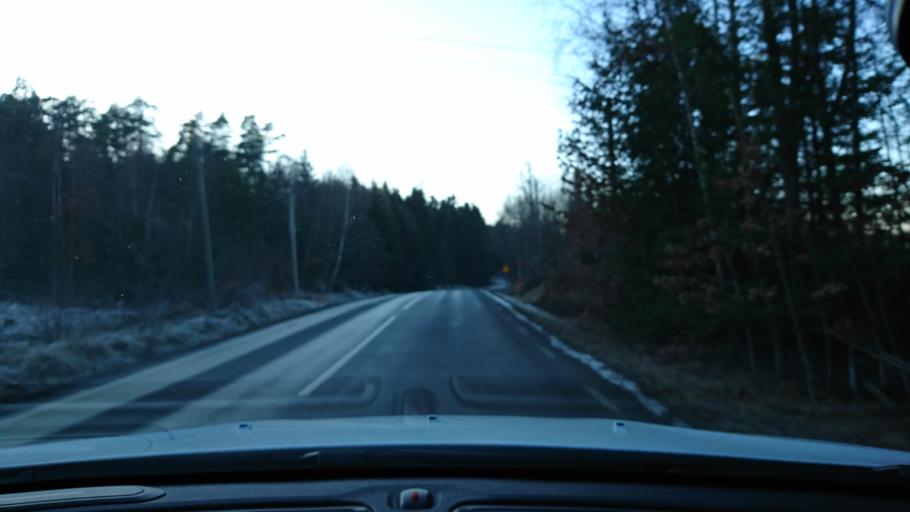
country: SE
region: Vaestra Goetaland
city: Svanesund
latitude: 58.1488
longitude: 11.8717
